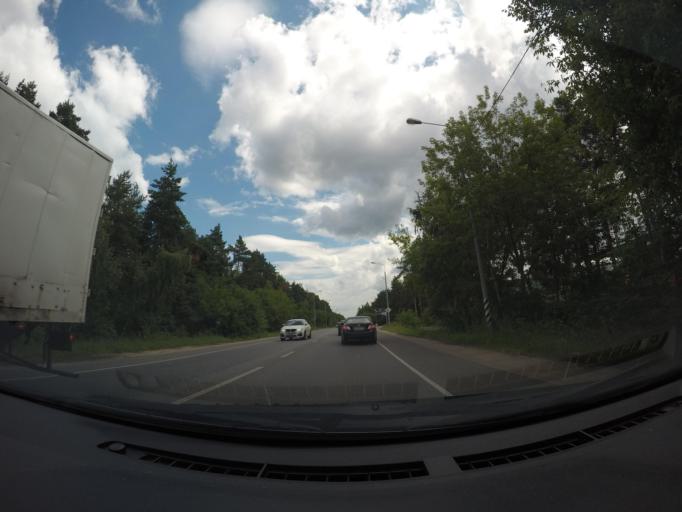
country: RU
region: Moskovskaya
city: Rodniki
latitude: 55.6560
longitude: 38.0742
